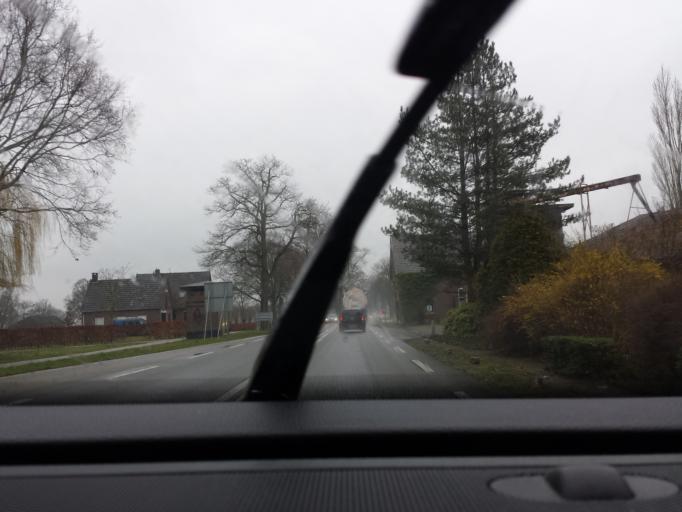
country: NL
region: Gelderland
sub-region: Gemeente Bronckhorst
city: Hengelo
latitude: 52.0698
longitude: 6.3102
